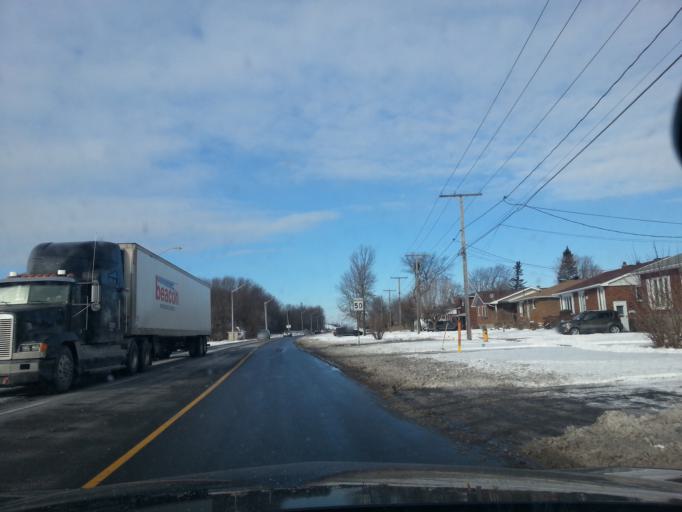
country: CA
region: Ontario
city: Cornwall
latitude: 45.0359
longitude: -74.7249
